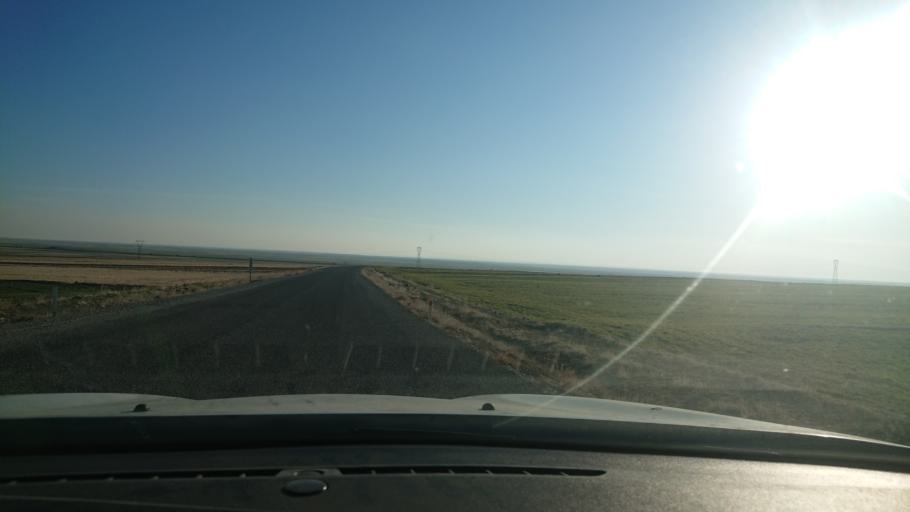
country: TR
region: Aksaray
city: Acipinar
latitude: 38.6768
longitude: 33.7316
